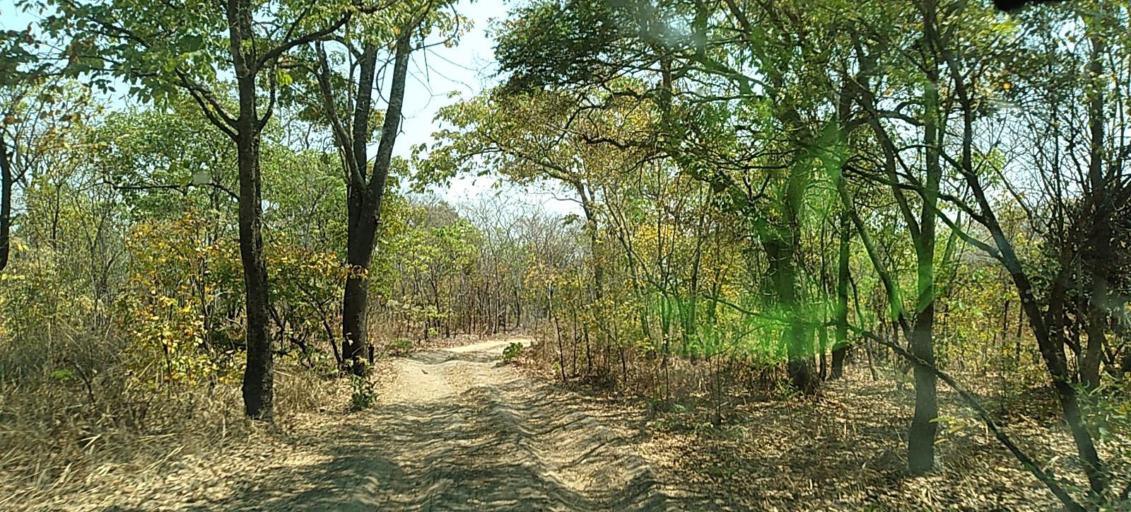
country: ZM
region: North-Western
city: Kalengwa
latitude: -13.1102
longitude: 24.6908
